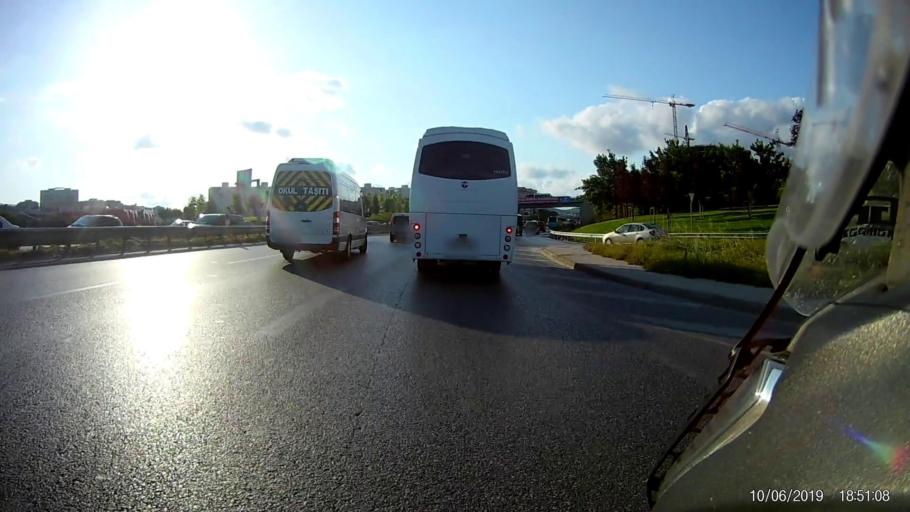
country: TR
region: Istanbul
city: Sancaktepe
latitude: 41.0324
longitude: 29.2570
